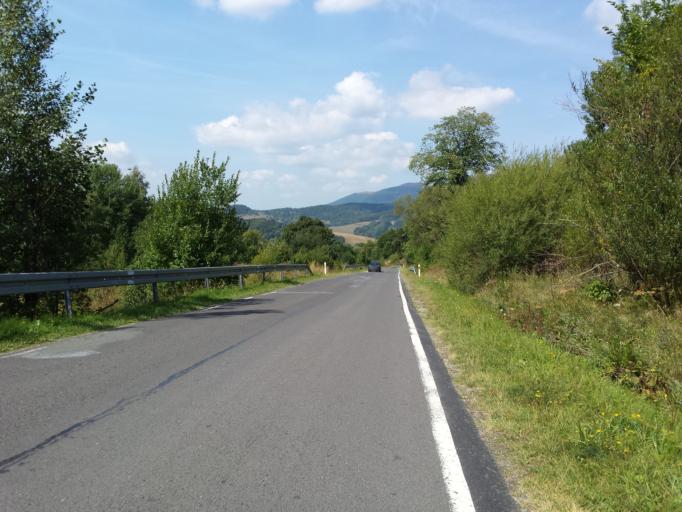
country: PL
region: Subcarpathian Voivodeship
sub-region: Powiat bieszczadzki
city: Lutowiska
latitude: 49.1263
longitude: 22.5899
